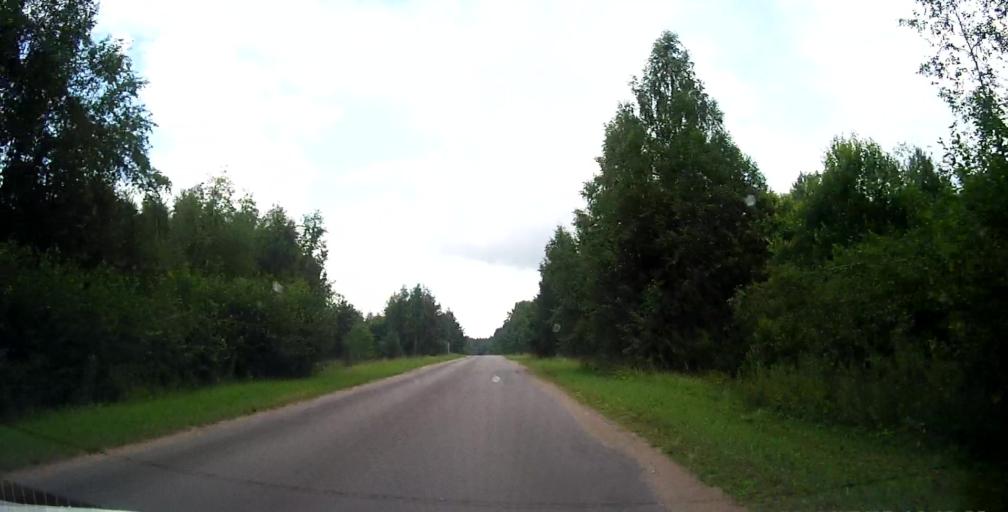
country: RU
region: Smolensk
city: Demidov
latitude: 55.4712
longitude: 31.6226
